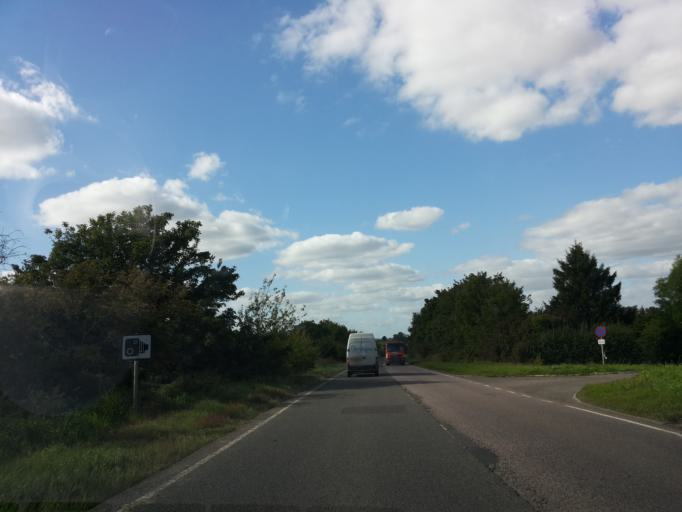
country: GB
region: England
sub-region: Wiltshire
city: Chapmanslade
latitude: 51.2277
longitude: -2.2245
